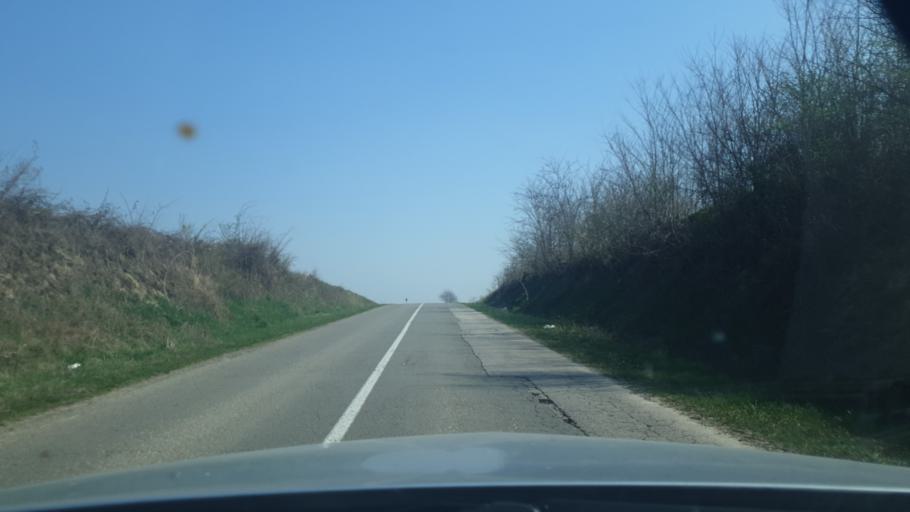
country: RS
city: Sasinci
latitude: 45.0479
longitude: 19.6977
